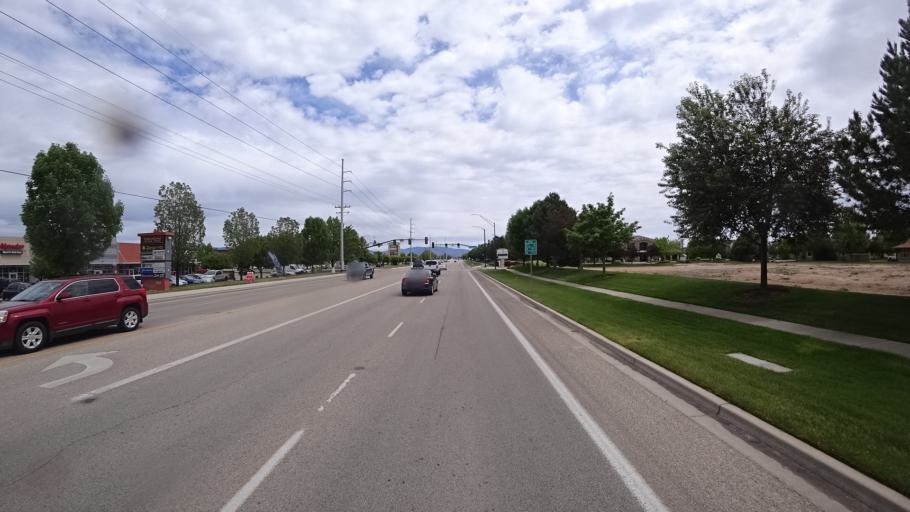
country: US
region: Idaho
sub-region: Ada County
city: Meridian
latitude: 43.5902
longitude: -116.3691
